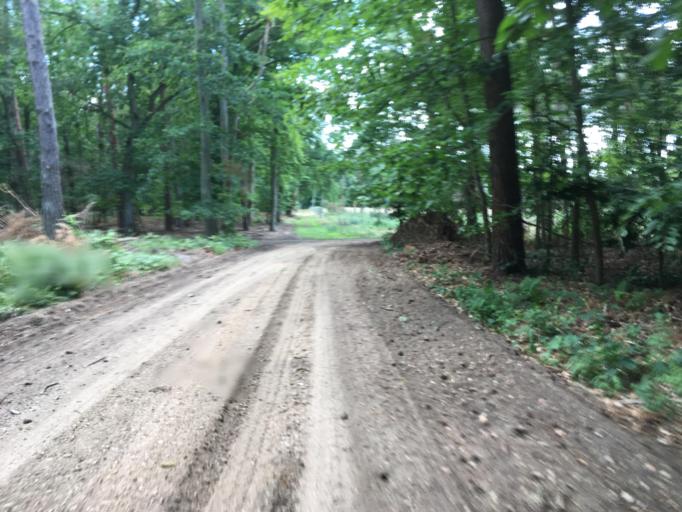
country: DE
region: Brandenburg
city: Joachimsthal
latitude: 52.9147
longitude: 13.7427
